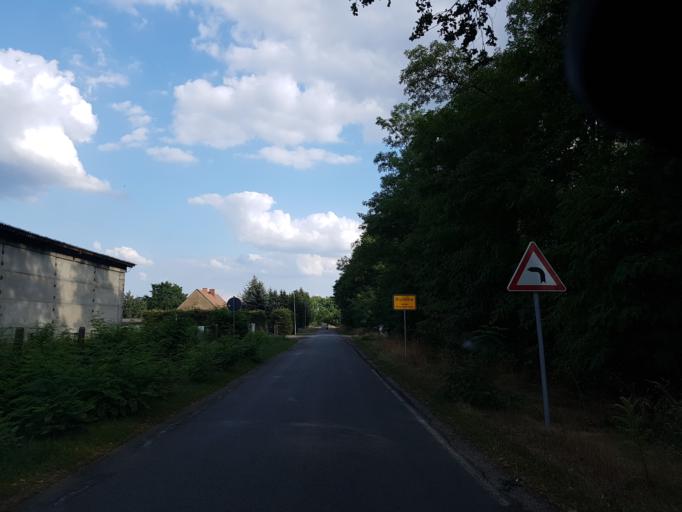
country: DE
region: Brandenburg
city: Bronkow
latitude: 51.6746
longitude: 13.9089
